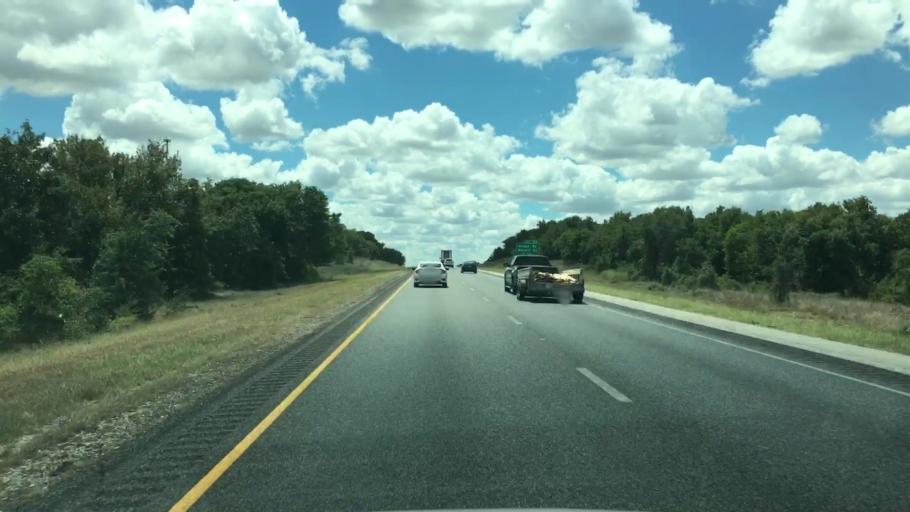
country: US
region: Texas
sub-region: Bexar County
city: Elmendorf
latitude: 29.1915
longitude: -98.4233
